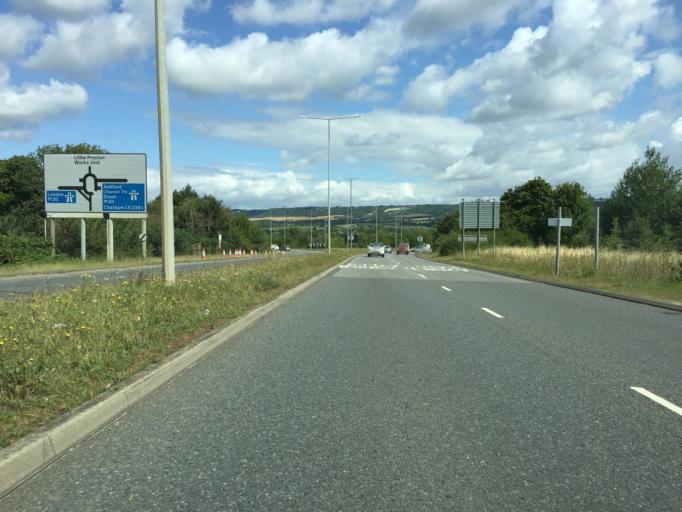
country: GB
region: England
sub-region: Kent
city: Aylesford
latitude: 51.2937
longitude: 0.4841
